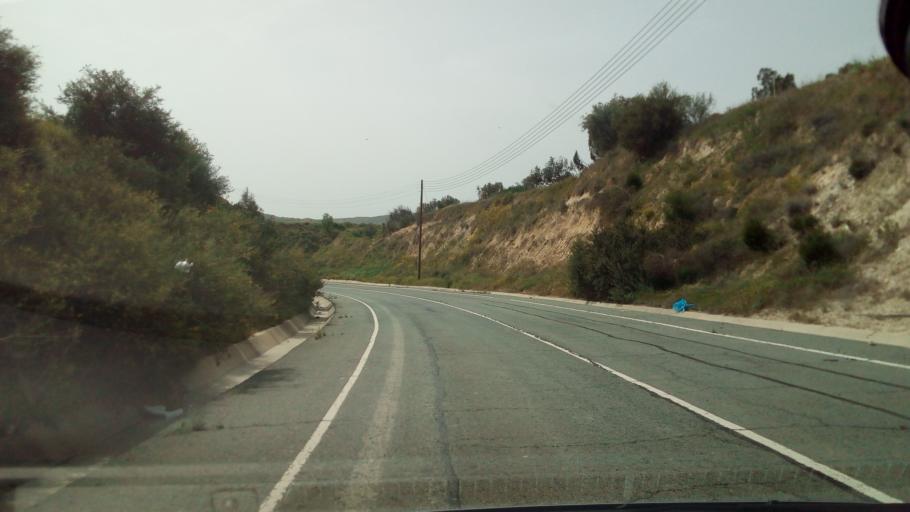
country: CY
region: Limassol
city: Pissouri
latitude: 34.6783
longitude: 32.7249
